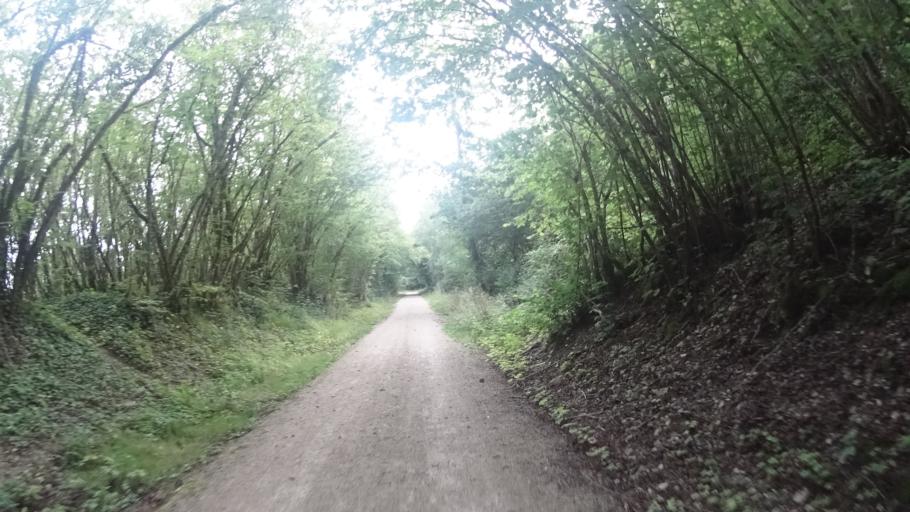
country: FR
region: Picardie
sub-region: Departement de l'Aisne
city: Origny-Sainte-Benoite
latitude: 49.8744
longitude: 3.5385
